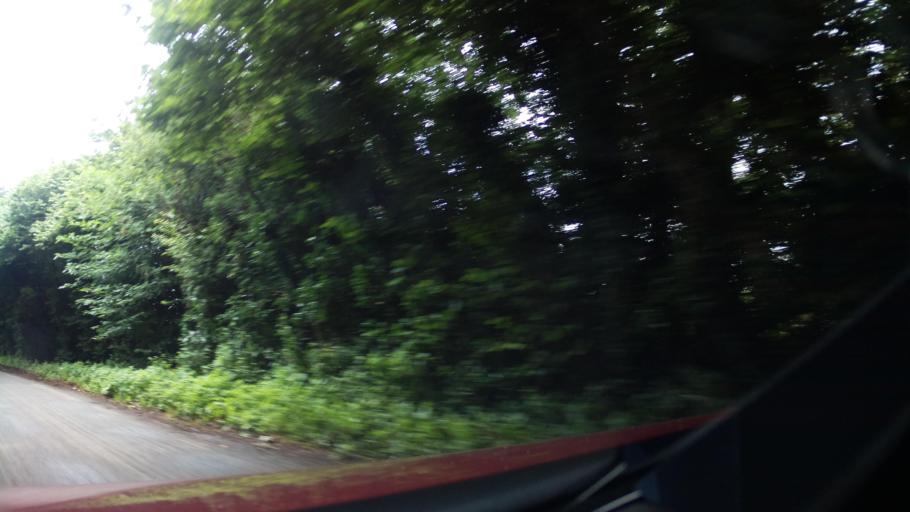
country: GB
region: England
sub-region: Somerset
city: Evercreech
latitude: 51.1783
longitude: -2.5082
